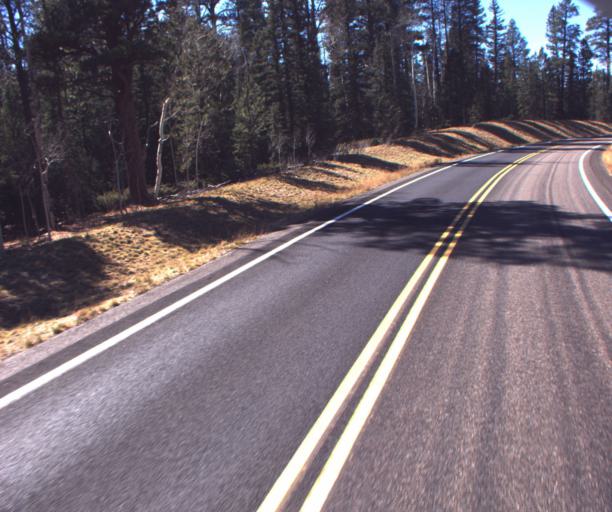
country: US
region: Arizona
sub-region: Coconino County
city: Grand Canyon
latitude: 36.5348
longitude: -112.1554
